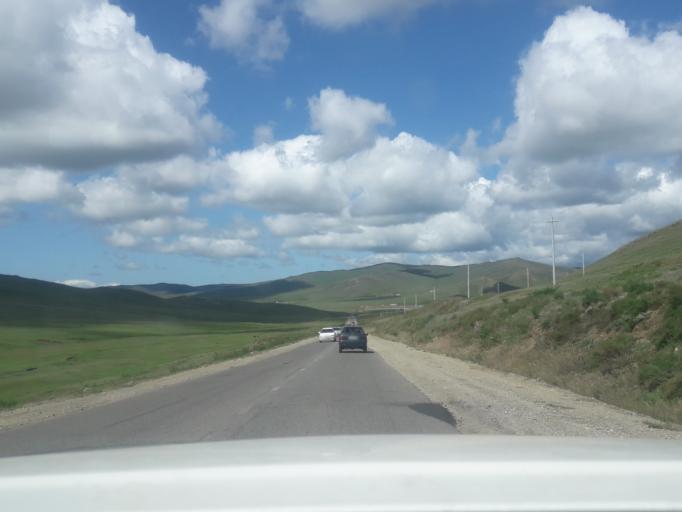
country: MN
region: Central Aimak
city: Ihsueuej
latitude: 48.1489
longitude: 106.4088
